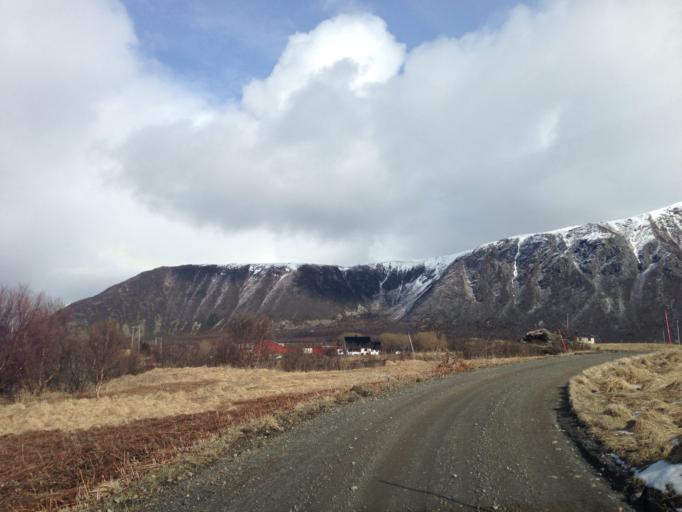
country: NO
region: Nordland
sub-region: Vagan
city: Kabelvag
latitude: 68.3912
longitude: 14.4532
